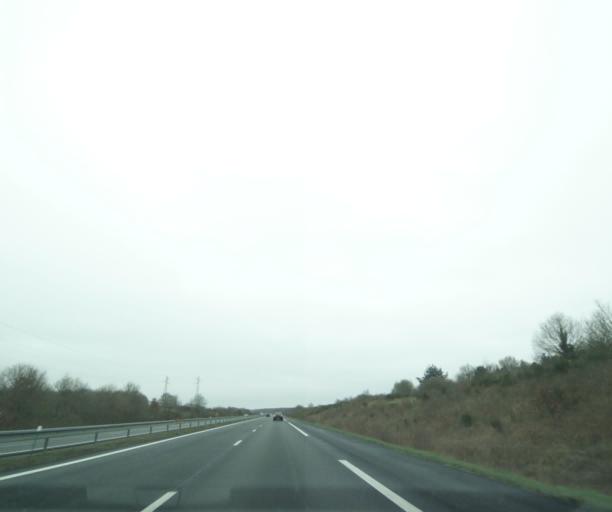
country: FR
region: Centre
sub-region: Departement du Loir-et-Cher
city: Theillay
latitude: 47.3064
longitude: 2.0458
